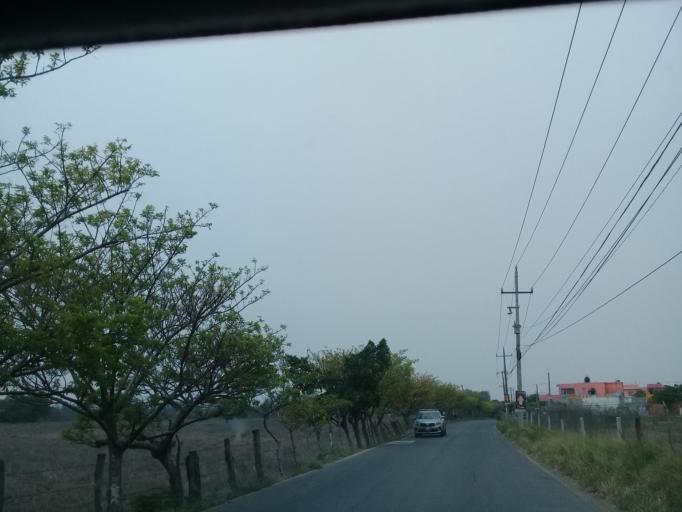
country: MX
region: Veracruz
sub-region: Veracruz
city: Las Amapolas
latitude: 19.1506
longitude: -96.2141
